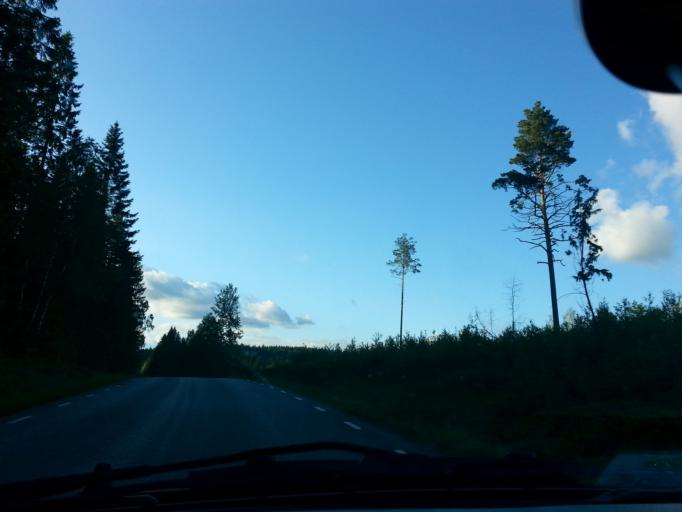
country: SE
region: Joenkoeping
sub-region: Gislaveds Kommun
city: Reftele
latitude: 57.2383
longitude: 13.6464
